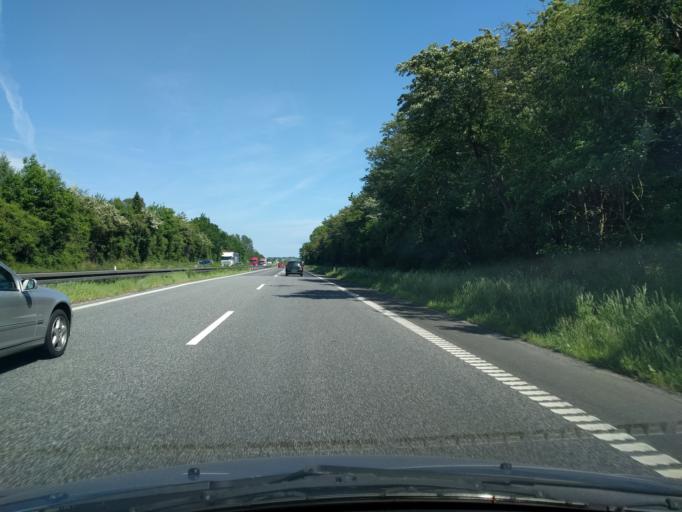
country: DK
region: Zealand
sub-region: Slagelse Kommune
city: Forlev
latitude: 55.3653
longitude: 11.2603
